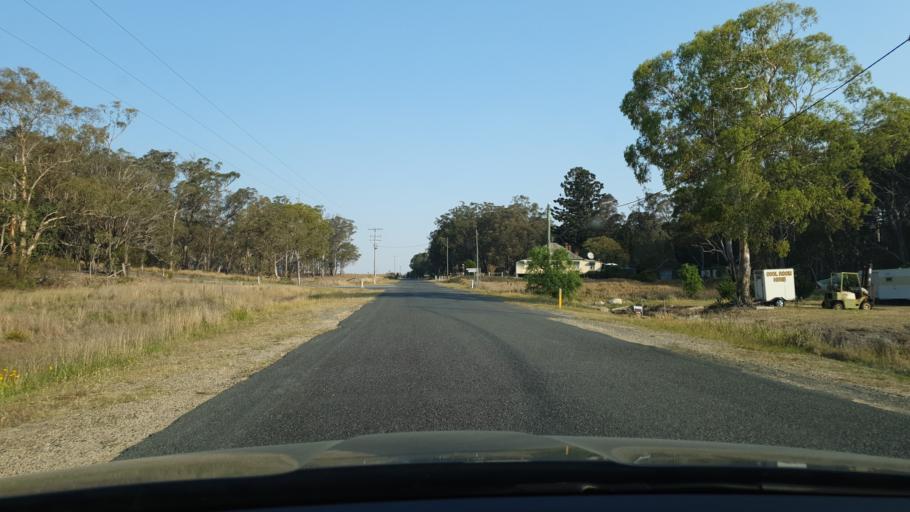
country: AU
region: New South Wales
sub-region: Tenterfield Municipality
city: Carrolls Creek
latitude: -28.6893
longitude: 152.0862
